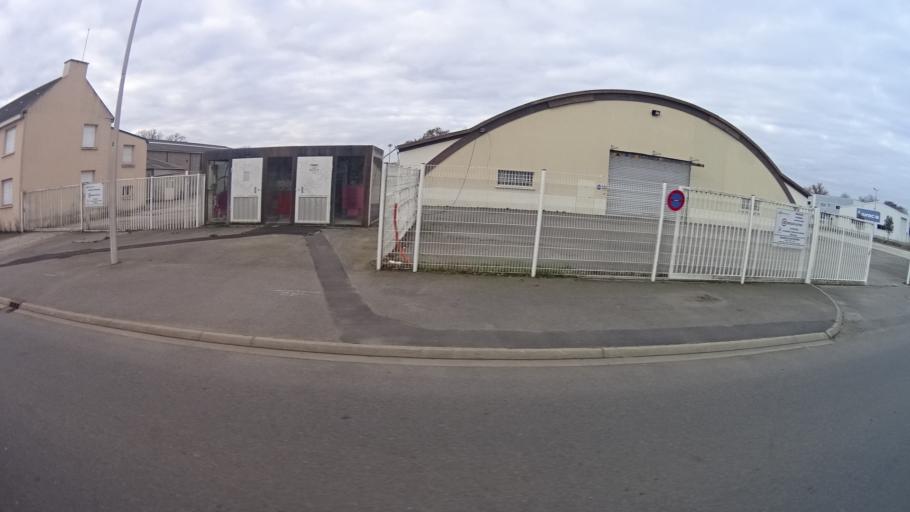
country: FR
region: Brittany
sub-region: Departement d'Ille-et-Vilaine
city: Redon
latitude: 47.6685
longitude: -2.0715
